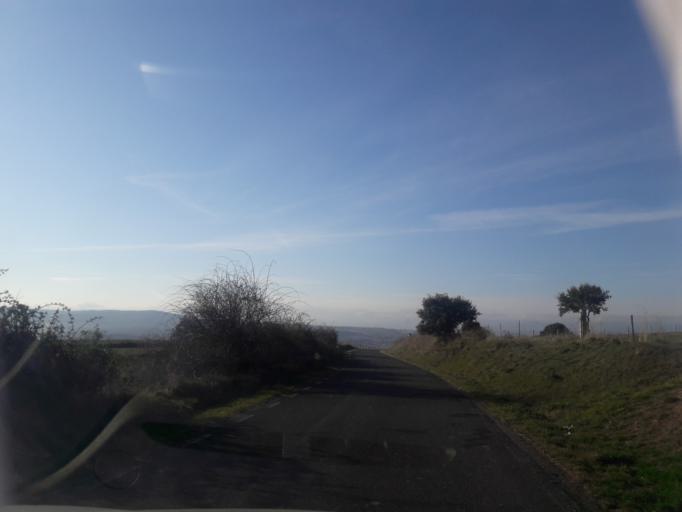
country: ES
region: Castille and Leon
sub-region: Provincia de Salamanca
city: Salvatierra de Tormes
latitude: 40.6051
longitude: -5.6010
